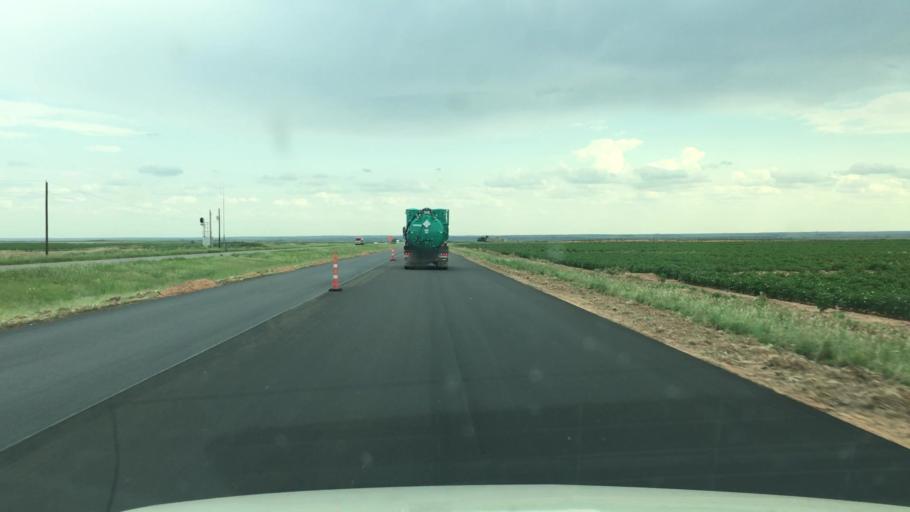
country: US
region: Texas
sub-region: Hall County
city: Memphis
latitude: 34.6274
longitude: -100.4749
